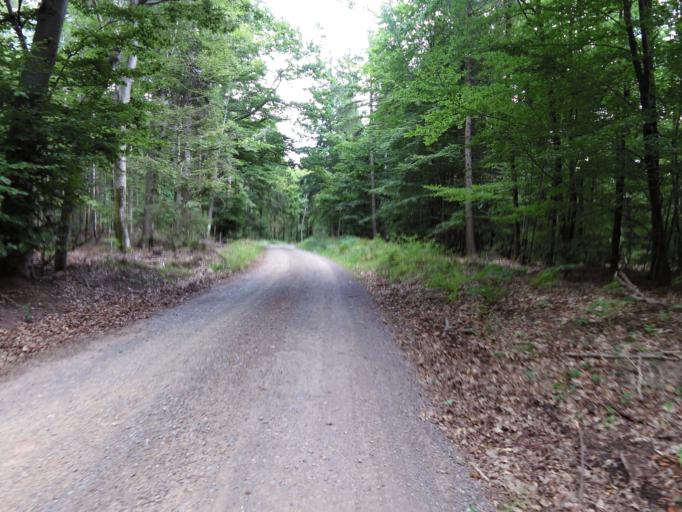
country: DE
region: Rheinland-Pfalz
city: Elmstein
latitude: 49.3893
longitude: 7.9376
